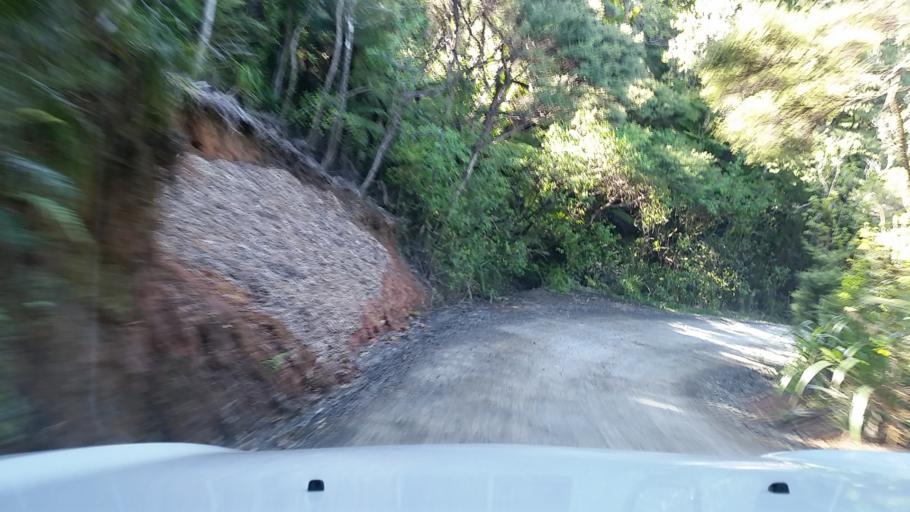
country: NZ
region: Auckland
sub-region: Auckland
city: Titirangi
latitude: -37.0310
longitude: 174.5199
